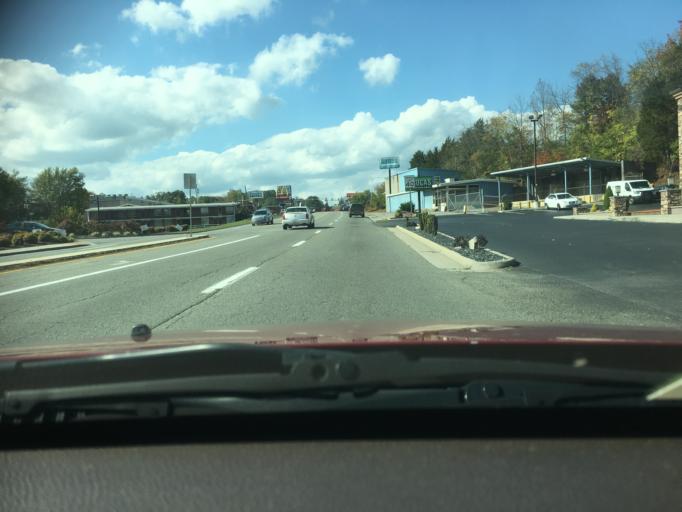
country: US
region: Virginia
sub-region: Pulaski County
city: Fairlawn
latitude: 37.1410
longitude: -80.5773
